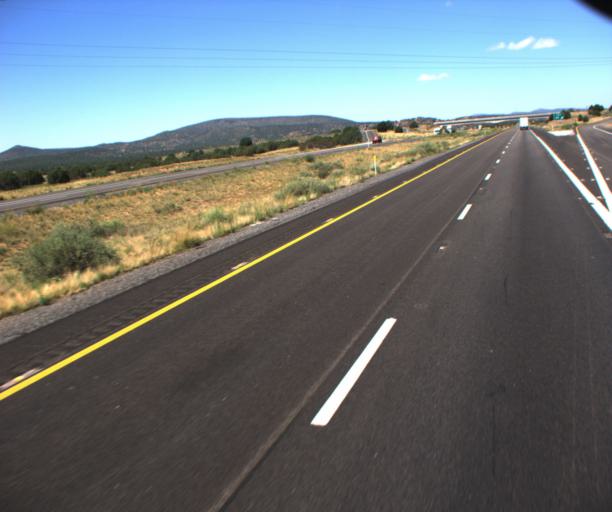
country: US
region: Arizona
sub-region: Mohave County
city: Peach Springs
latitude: 35.1910
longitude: -113.3604
